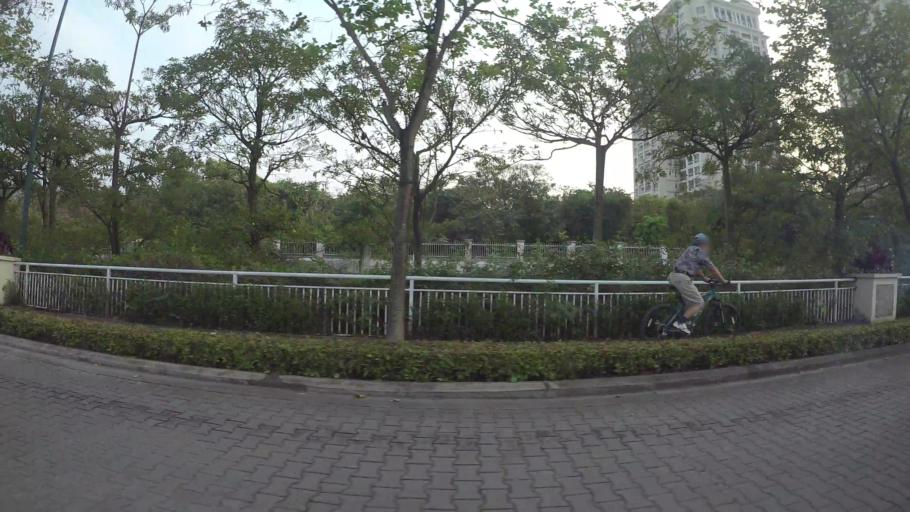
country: VN
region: Ha Noi
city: Tay Ho
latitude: 21.0791
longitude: 105.7943
